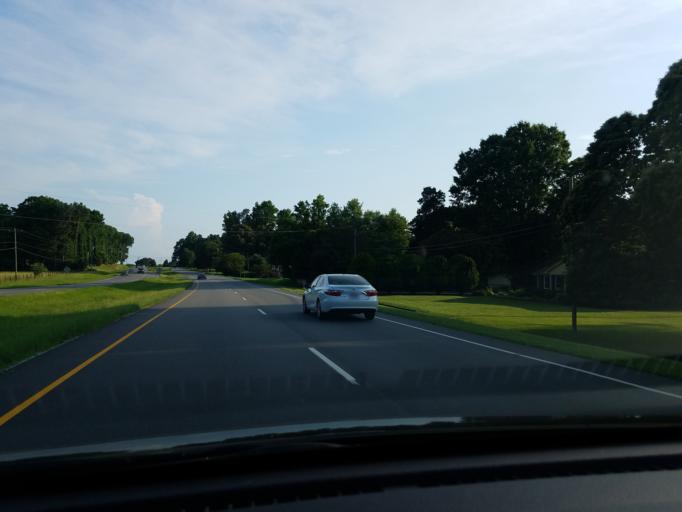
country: US
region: North Carolina
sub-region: Durham County
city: Gorman
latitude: 36.1161
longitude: -78.9040
